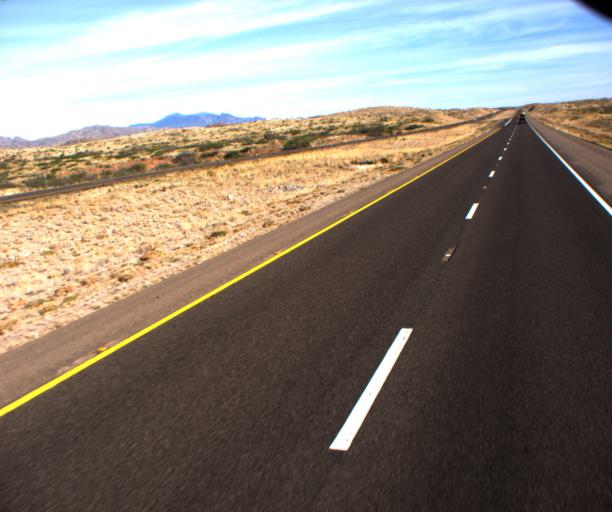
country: US
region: Arizona
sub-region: Cochise County
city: Willcox
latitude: 32.4146
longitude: -109.6621
